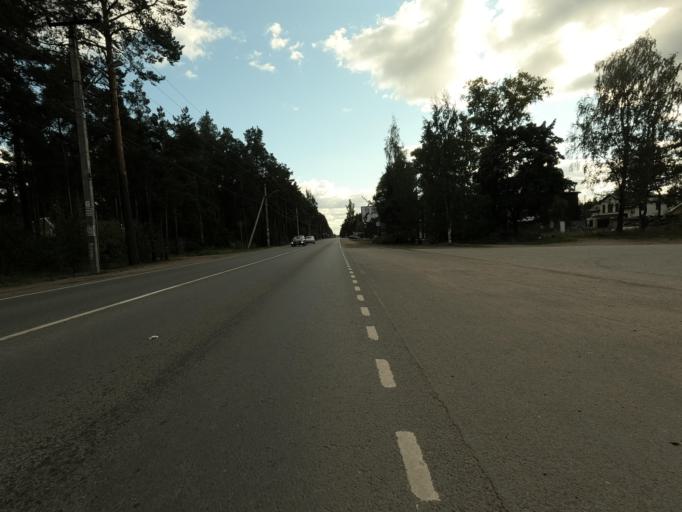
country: RU
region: Leningrad
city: Vsevolozhsk
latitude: 60.0002
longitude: 30.6617
